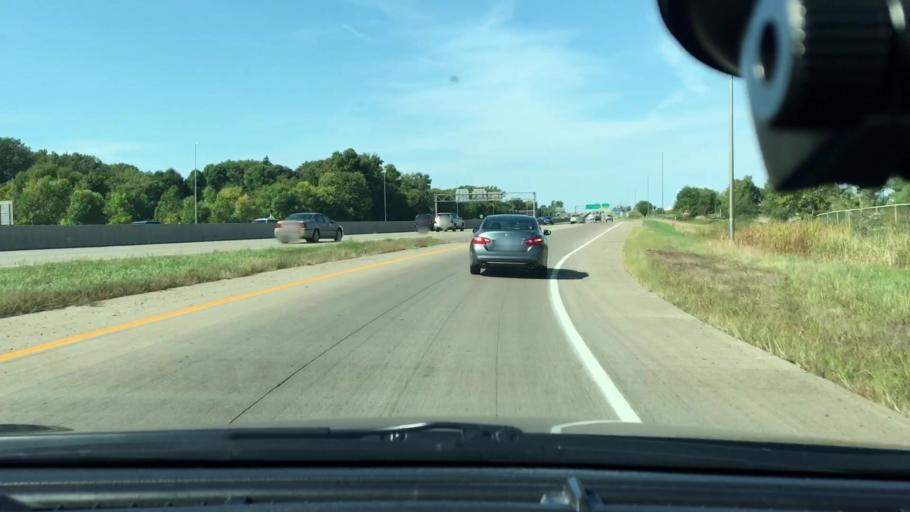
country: US
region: Minnesota
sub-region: Hennepin County
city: Osseo
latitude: 45.0846
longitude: -93.4058
